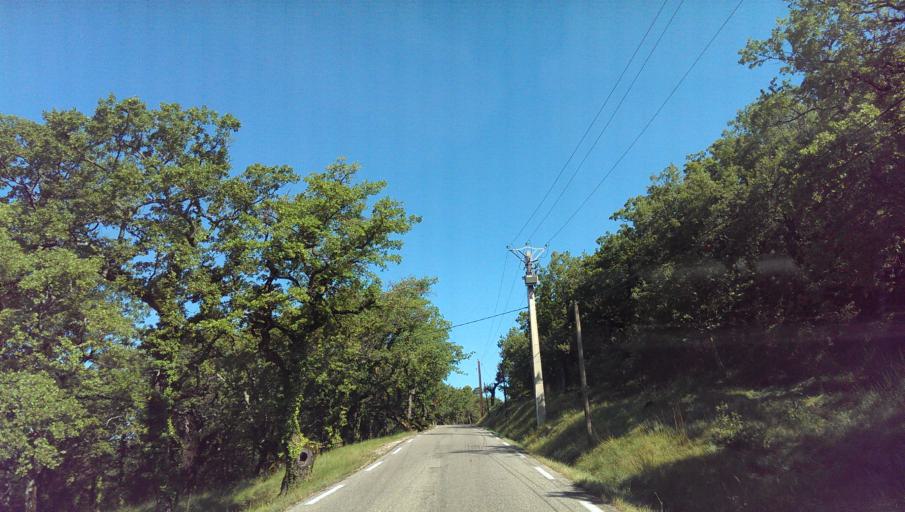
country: FR
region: Provence-Alpes-Cote d'Azur
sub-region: Departement du Vaucluse
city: Gordes
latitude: 43.9500
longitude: 5.2098
